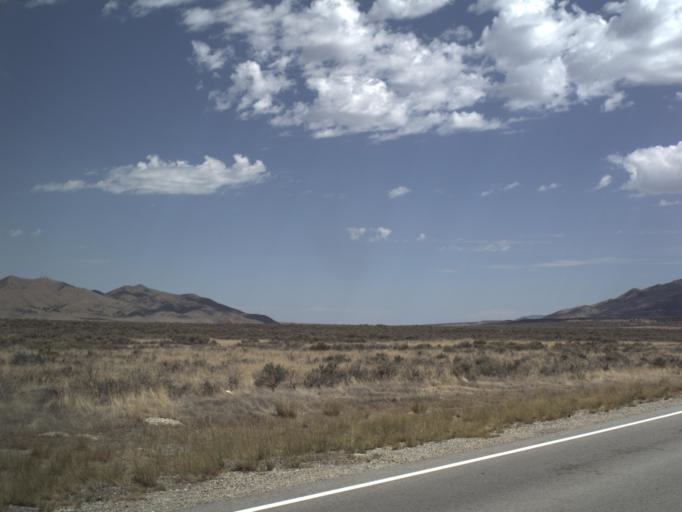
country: US
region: Utah
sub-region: Tooele County
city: Tooele
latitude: 40.3737
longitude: -112.3969
